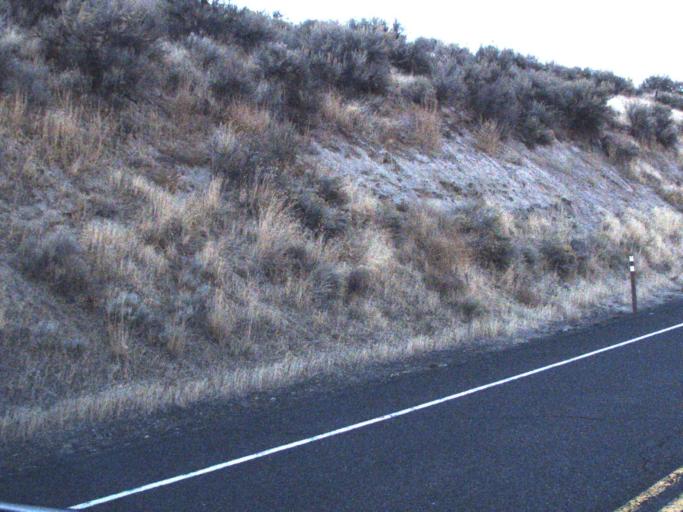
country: US
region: Washington
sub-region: Franklin County
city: Connell
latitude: 46.6732
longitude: -118.5450
